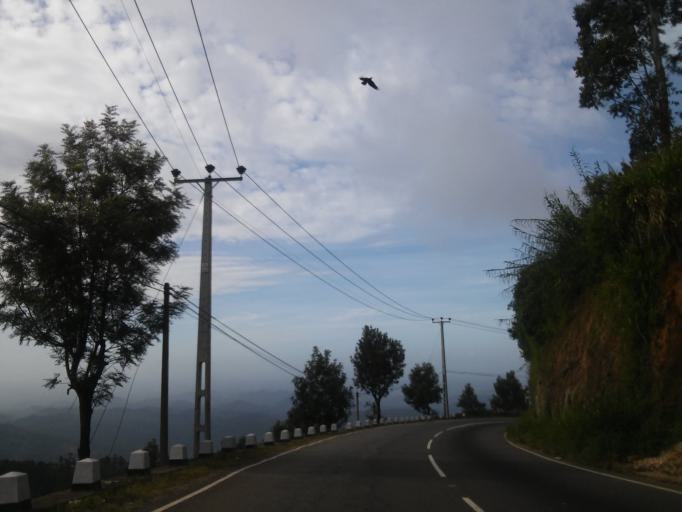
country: LK
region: Uva
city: Haputale
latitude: 6.7643
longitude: 80.9535
